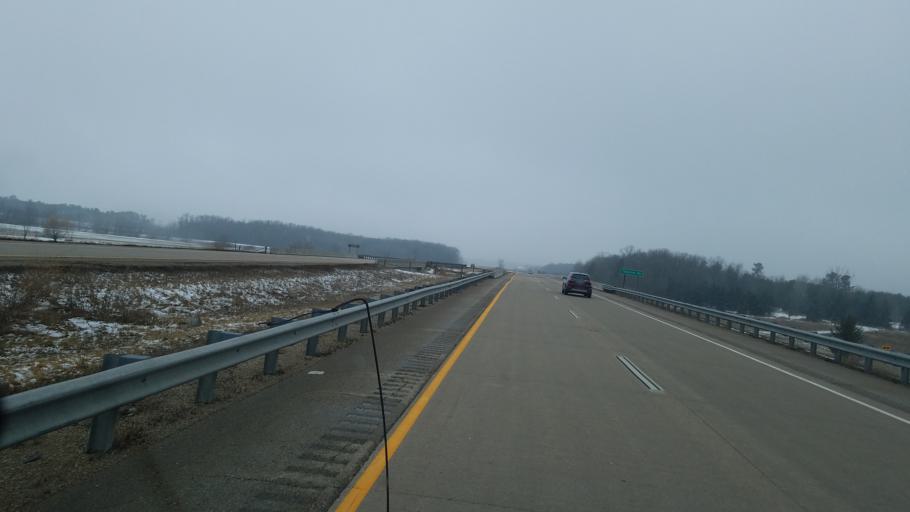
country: US
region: Wisconsin
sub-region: Winnebago County
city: Winneconne
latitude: 44.2342
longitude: -88.7642
